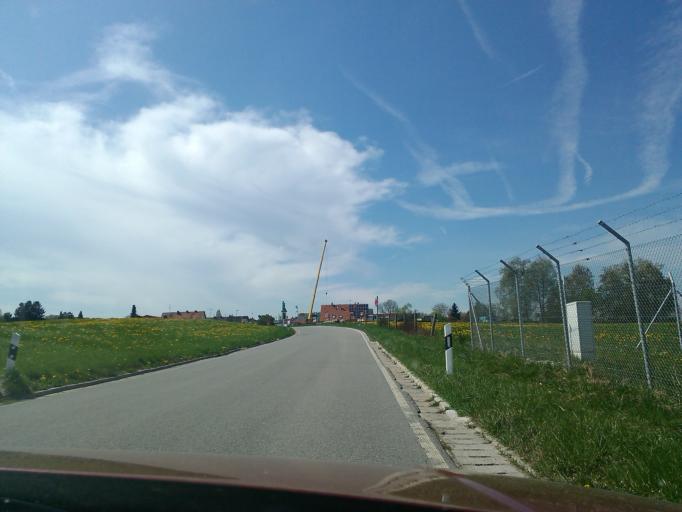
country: DE
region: Bavaria
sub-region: Upper Bavaria
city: Wessling
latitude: 48.0739
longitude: 11.2719
